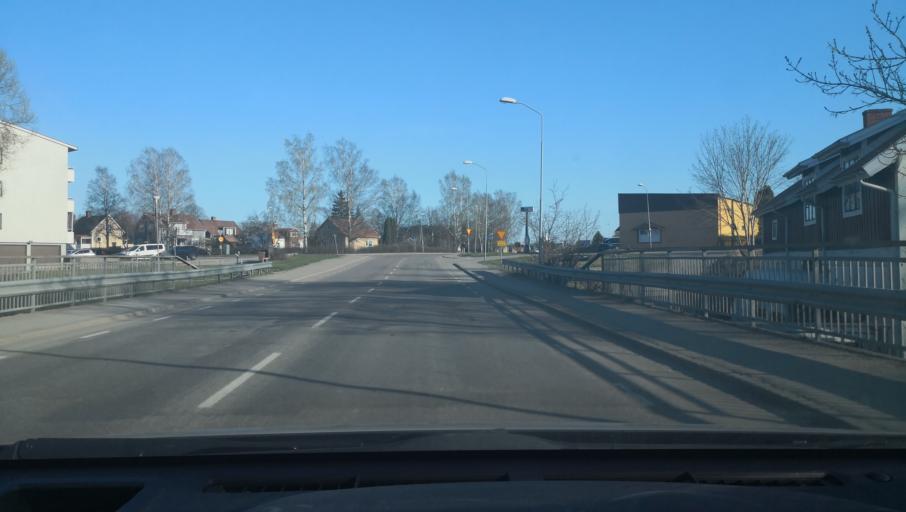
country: SE
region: Uppsala
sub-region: Heby Kommun
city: Heby
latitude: 59.9375
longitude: 16.8669
